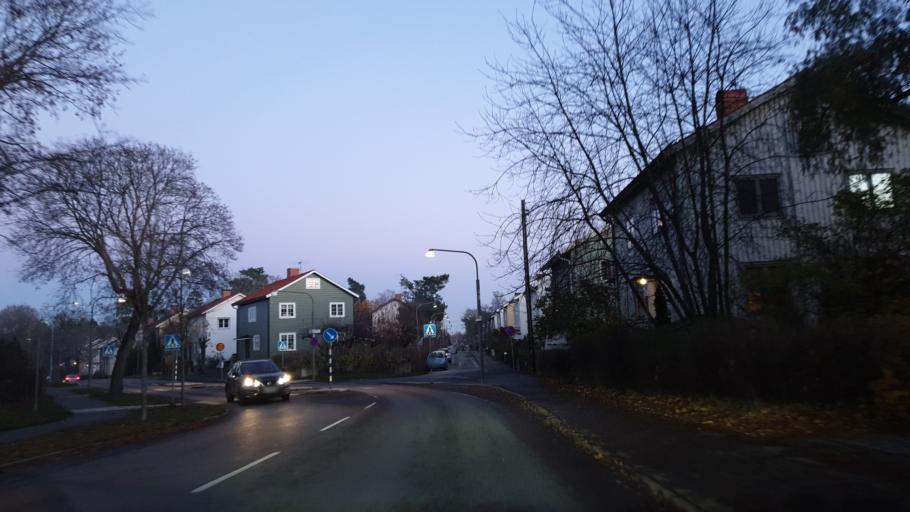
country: SE
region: Stockholm
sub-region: Stockholms Kommun
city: Bromma
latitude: 59.3293
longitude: 17.9292
